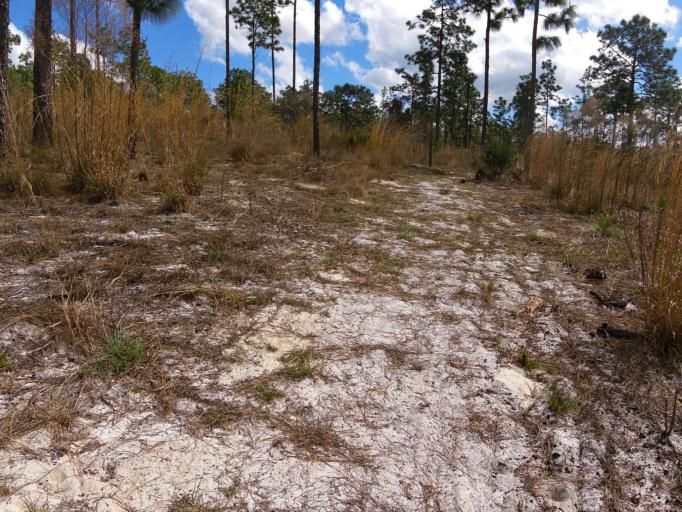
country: US
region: Florida
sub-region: Putnam County
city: Interlachen
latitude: 29.7809
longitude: -81.8731
